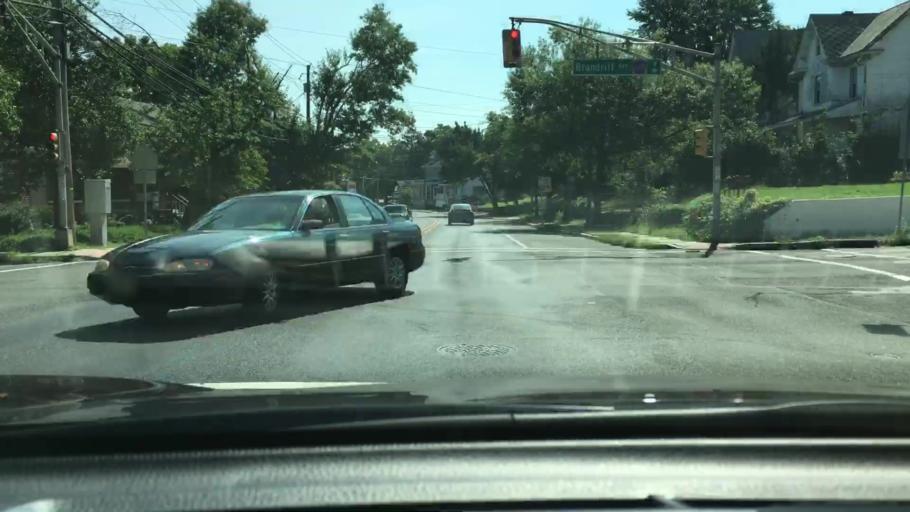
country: US
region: New Jersey
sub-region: Cumberland County
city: Millville
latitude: 39.3956
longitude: -75.0443
